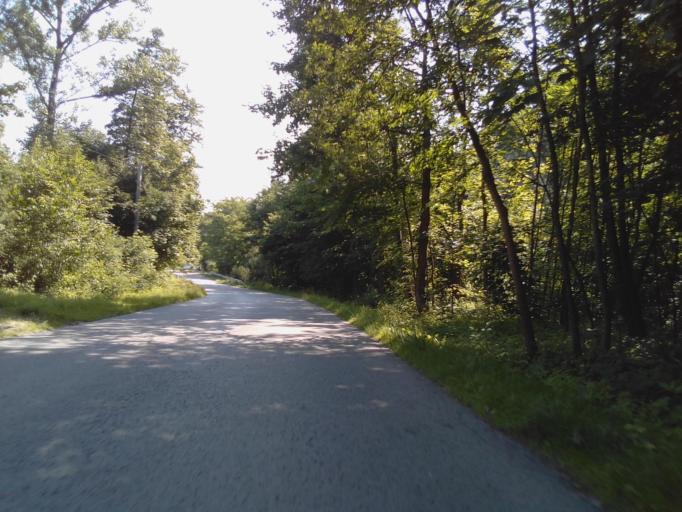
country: PL
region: Subcarpathian Voivodeship
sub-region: Powiat ropczycko-sedziszowski
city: Zagorzyce
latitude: 50.0295
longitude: 21.6449
